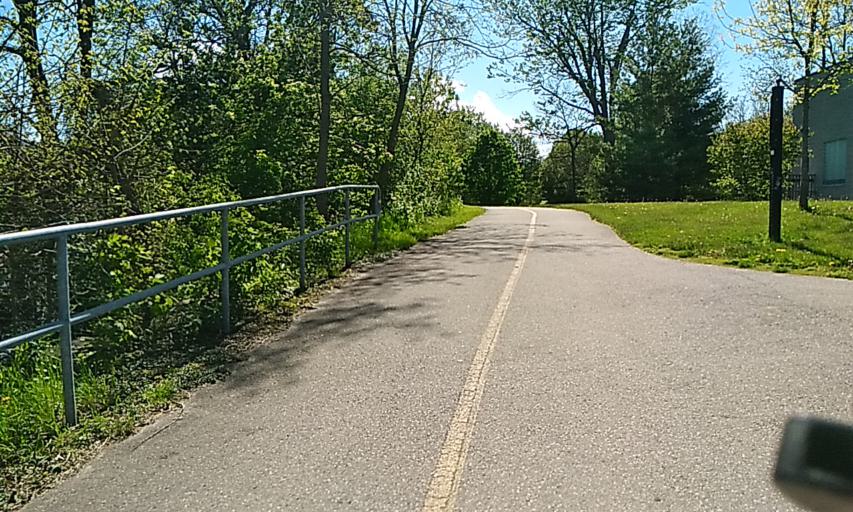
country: CA
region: Ontario
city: London
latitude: 42.9742
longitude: -81.2403
